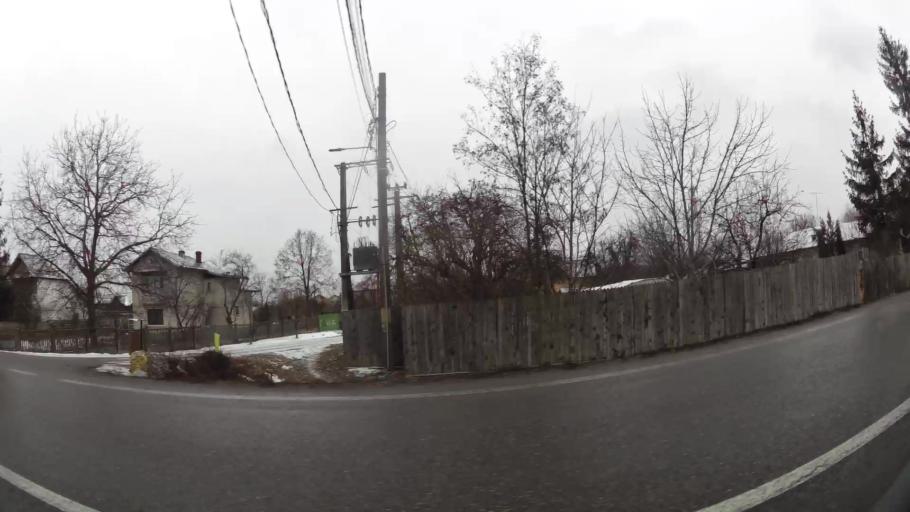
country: RO
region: Dambovita
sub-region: Comuna Aninoasa
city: Viforata
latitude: 44.9446
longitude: 25.4851
